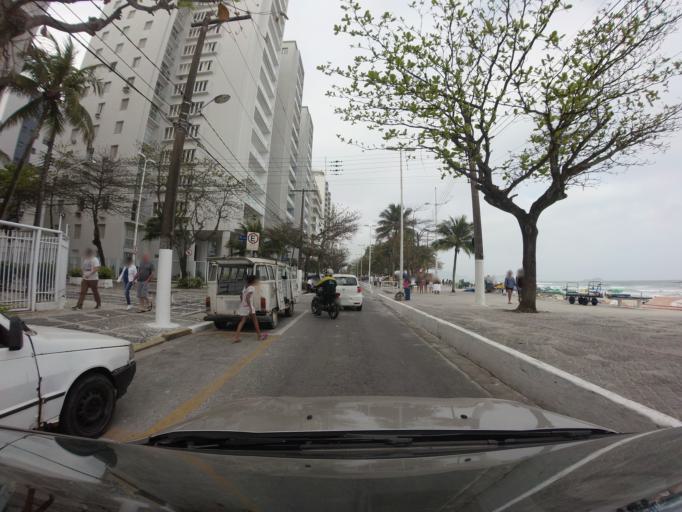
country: BR
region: Sao Paulo
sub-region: Guaruja
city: Guaruja
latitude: -23.9987
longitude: -46.2600
